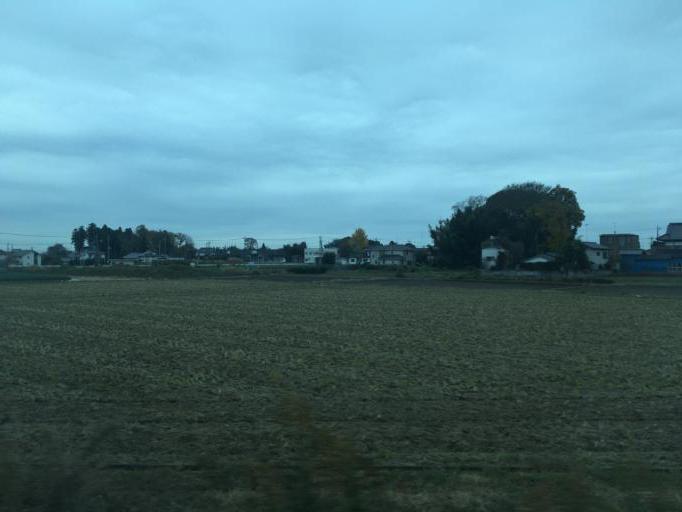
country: JP
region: Ibaraki
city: Shimodate
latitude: 36.3003
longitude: 139.9507
